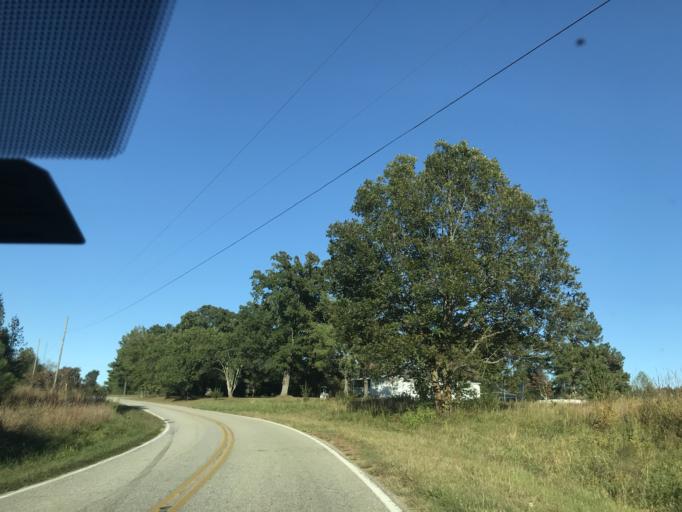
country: US
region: South Carolina
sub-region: Spartanburg County
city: Mayo
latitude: 35.1219
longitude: -81.7914
